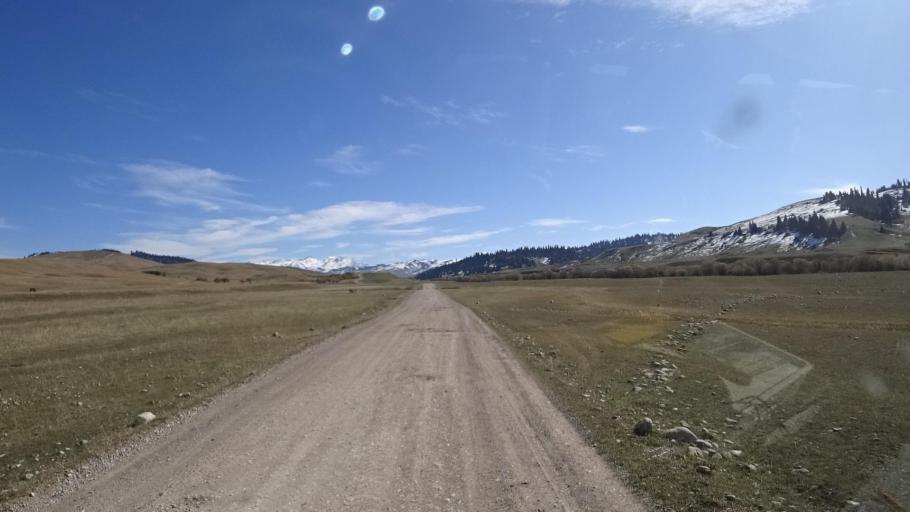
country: KZ
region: Almaty Oblysy
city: Kegen
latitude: 42.7399
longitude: 79.0057
